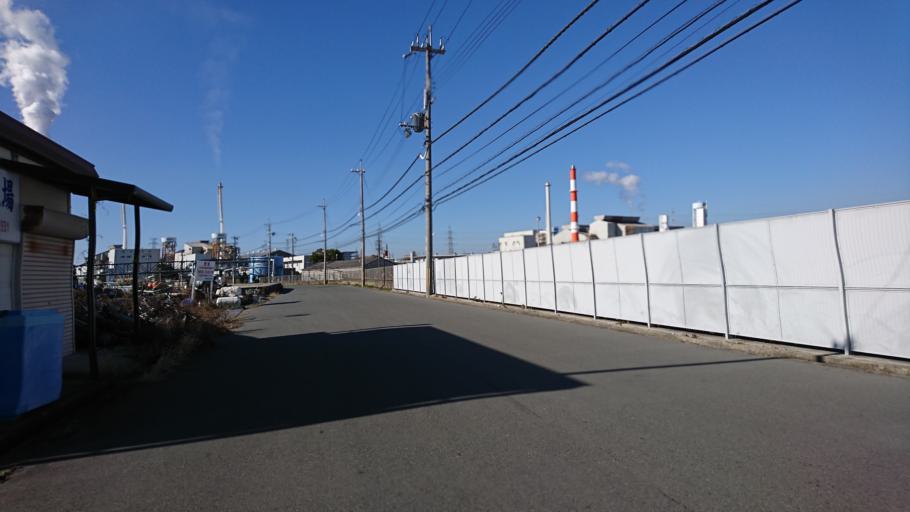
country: JP
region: Hyogo
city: Kakogawacho-honmachi
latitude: 34.7618
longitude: 134.7750
